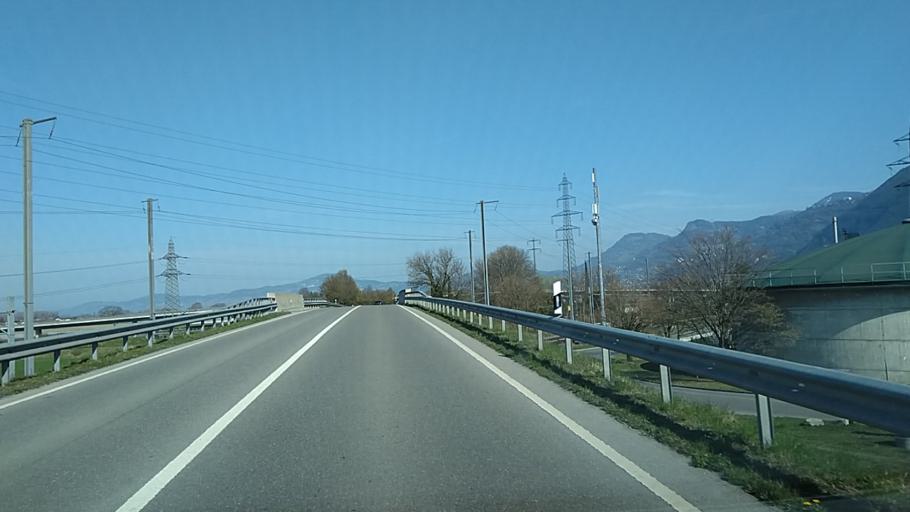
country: CH
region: Vaud
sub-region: Aigle District
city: Villeneuve
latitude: 46.3678
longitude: 6.9247
